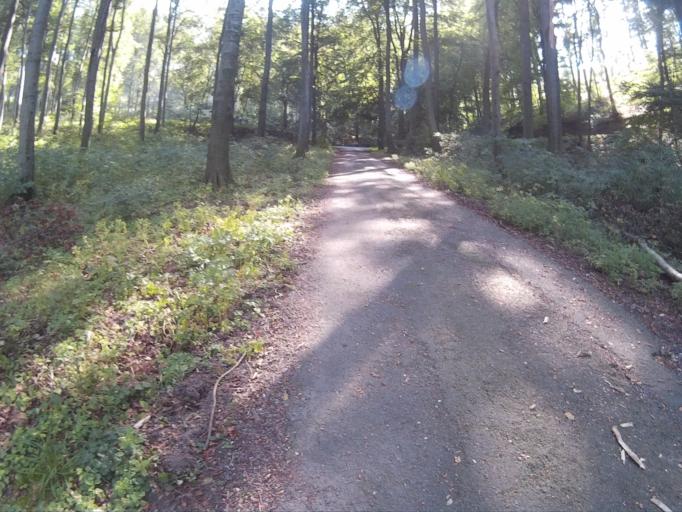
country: HU
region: Vas
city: Koszeg
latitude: 47.3856
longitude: 16.5000
